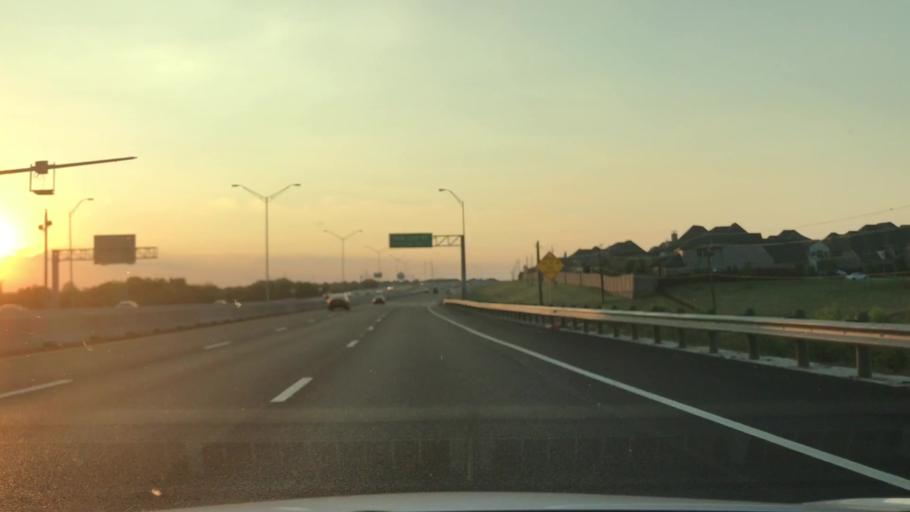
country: US
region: Texas
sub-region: Dallas County
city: Coppell
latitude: 32.9019
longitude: -96.9839
